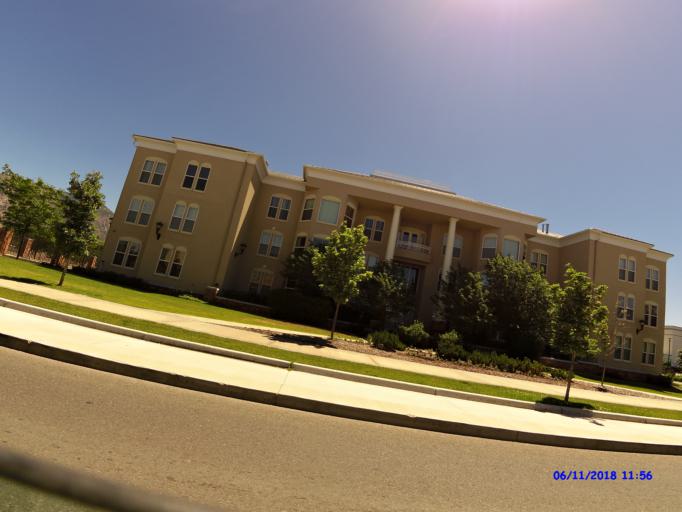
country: US
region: Utah
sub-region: Weber County
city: Ogden
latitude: 41.2296
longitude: -111.9731
